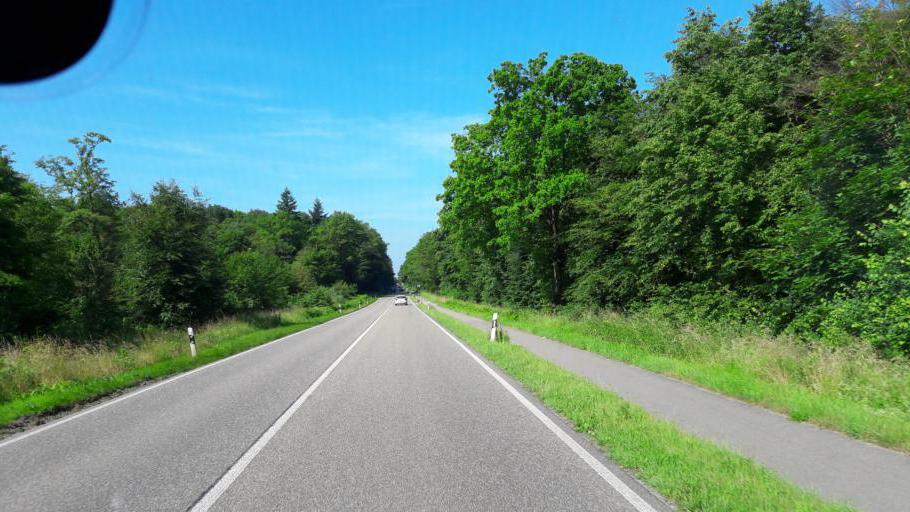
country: DE
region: Baden-Wuerttemberg
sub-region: Karlsruhe Region
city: Malsch
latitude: 48.9178
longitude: 8.3486
